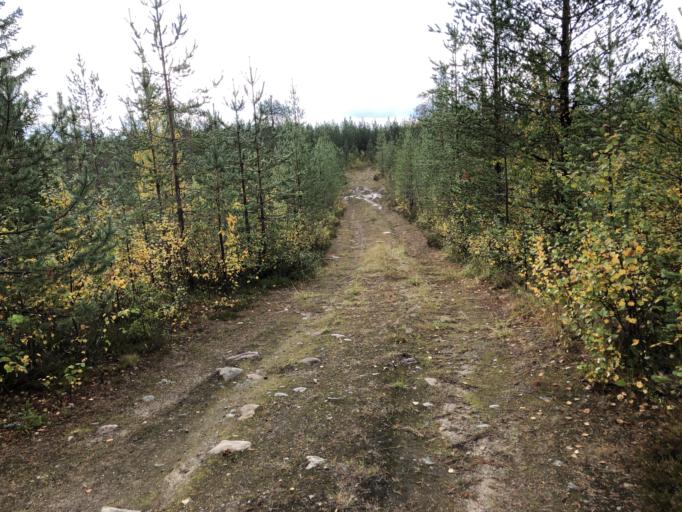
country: FI
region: Northern Ostrobothnia
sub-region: Koillismaa
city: Kuusamo
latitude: 65.9086
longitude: 28.8721
